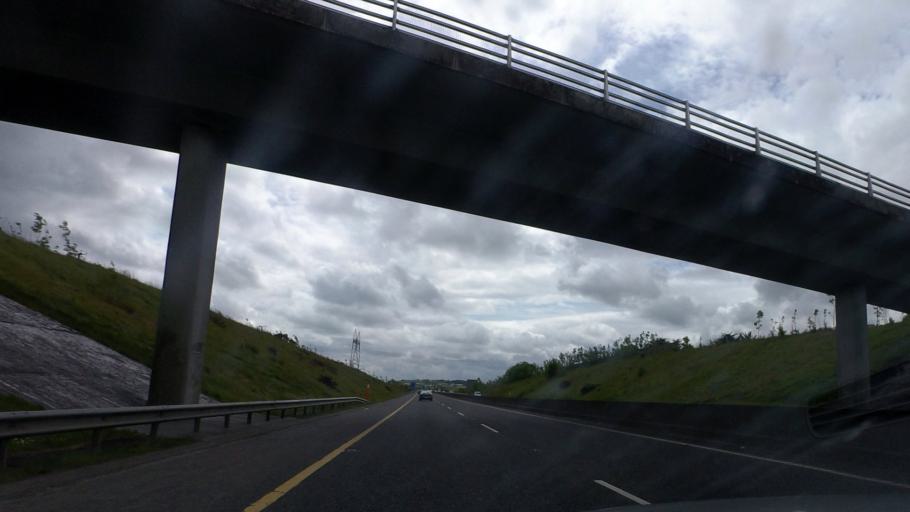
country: IE
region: Munster
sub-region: An Clar
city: Newmarket on Fergus
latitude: 52.8070
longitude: -8.9298
